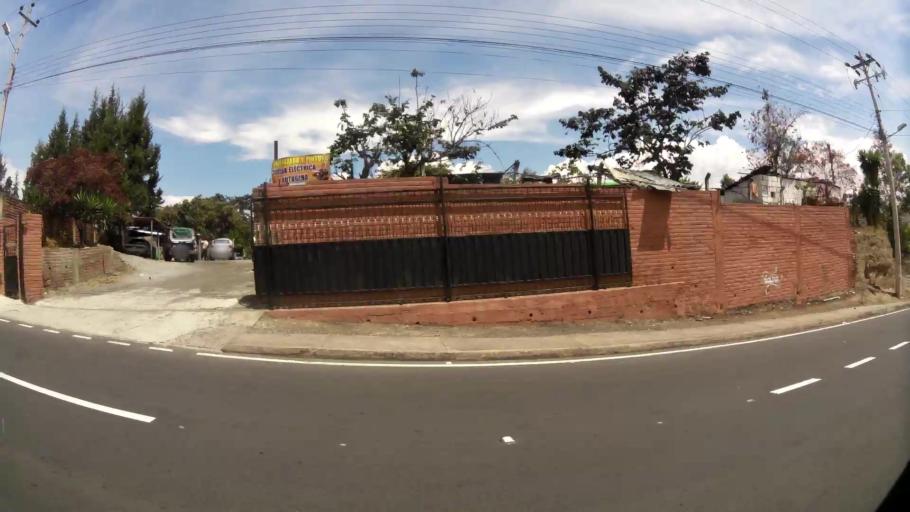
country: EC
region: Pichincha
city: Sangolqui
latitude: -0.2016
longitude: -78.3691
